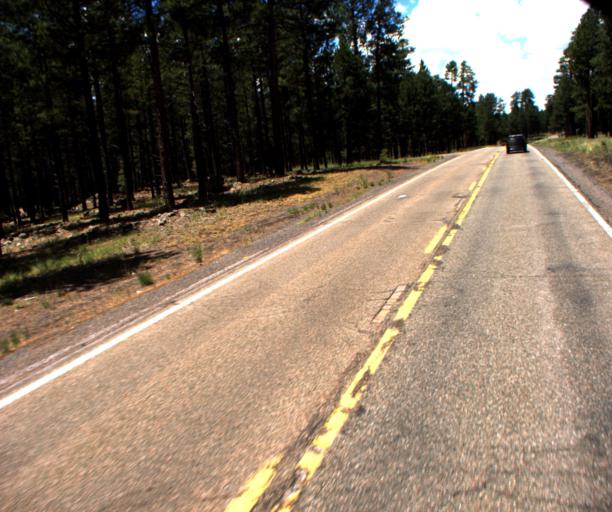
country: US
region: Arizona
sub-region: Coconino County
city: Parks
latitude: 35.3308
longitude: -111.7794
